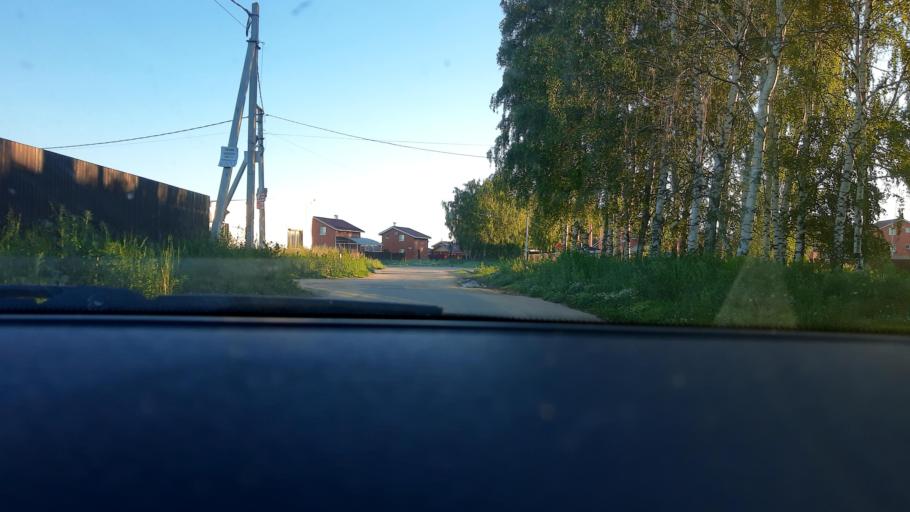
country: RU
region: Nizjnij Novgorod
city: Afonino
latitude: 56.1962
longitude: 44.0806
